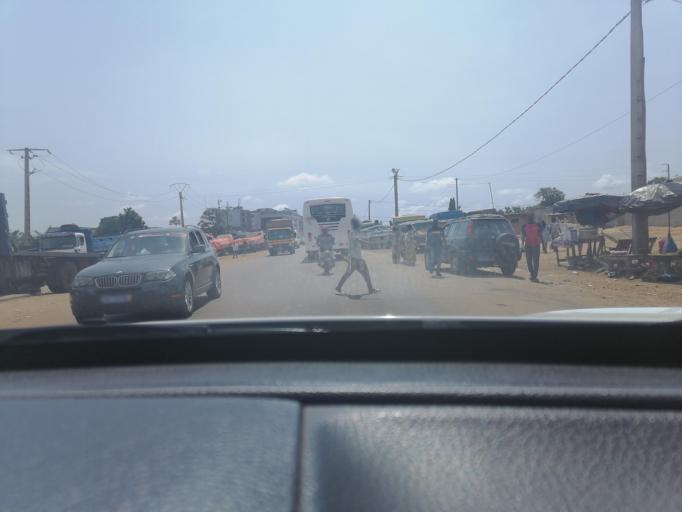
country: CI
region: Lagunes
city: Abidjan
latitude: 5.3510
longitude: -4.1041
